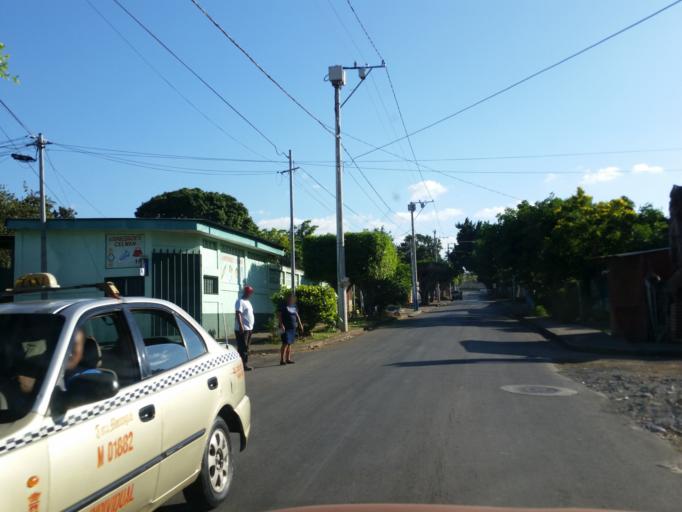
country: NI
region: Managua
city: Managua
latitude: 12.1178
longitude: -86.2938
